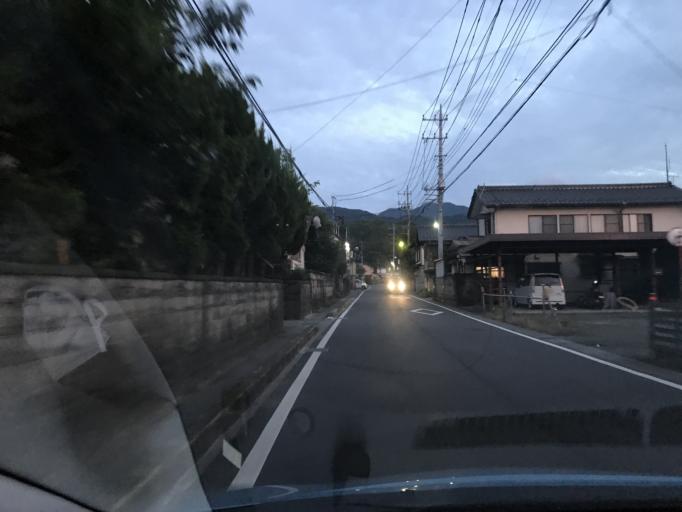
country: JP
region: Yamanashi
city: Ryuo
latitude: 35.5821
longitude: 138.5484
